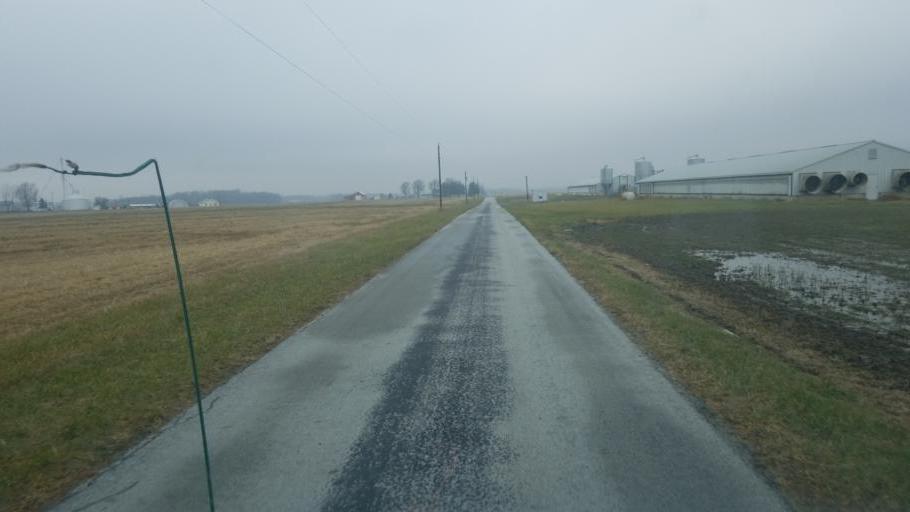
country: US
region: Ohio
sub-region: Hardin County
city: Forest
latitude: 40.6894
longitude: -83.4778
